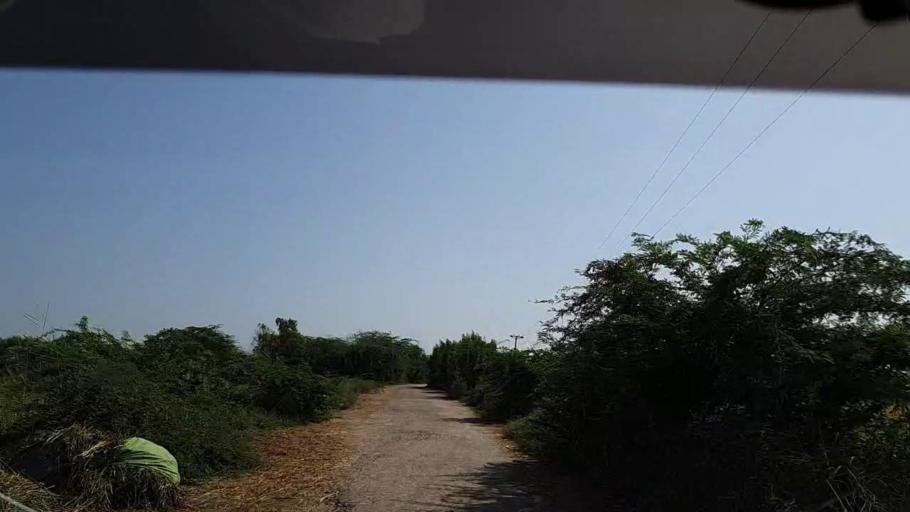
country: PK
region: Sindh
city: Badin
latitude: 24.6360
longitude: 68.7865
